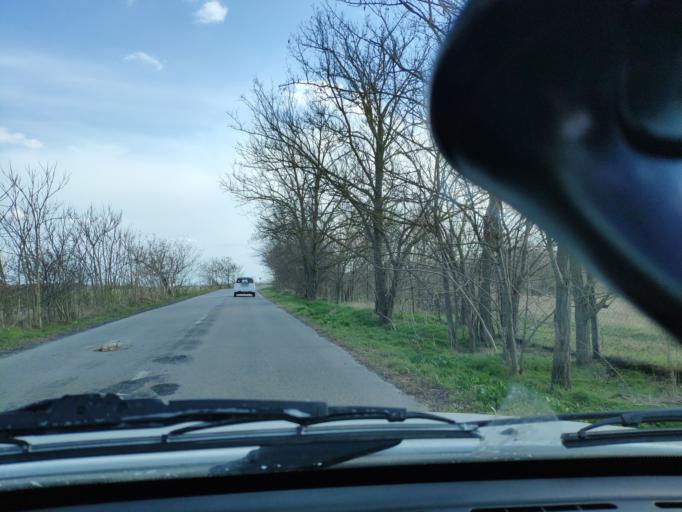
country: HU
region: Pest
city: Rackeve
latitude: 47.1461
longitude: 18.9108
